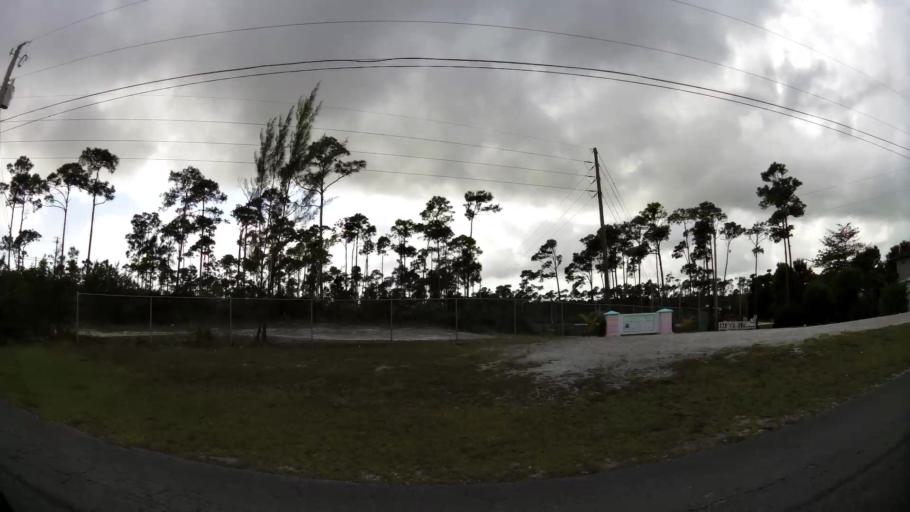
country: BS
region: Freeport
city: Freeport
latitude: 26.5300
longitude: -78.7021
